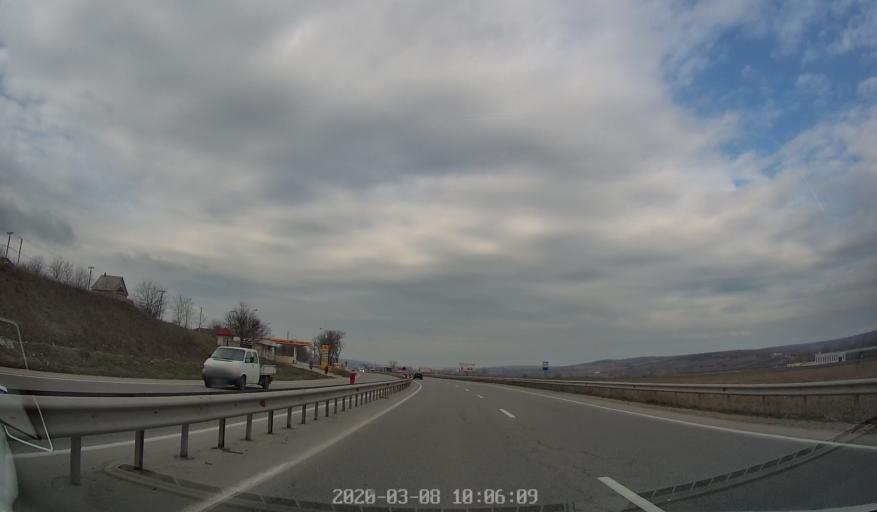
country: MD
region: Chisinau
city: Cricova
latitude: 47.1672
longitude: 28.8169
